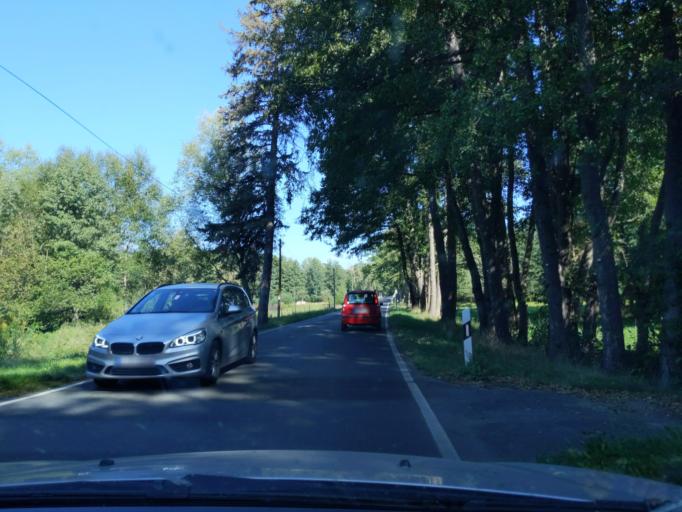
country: DE
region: Brandenburg
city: Burg
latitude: 51.8292
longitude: 14.1038
